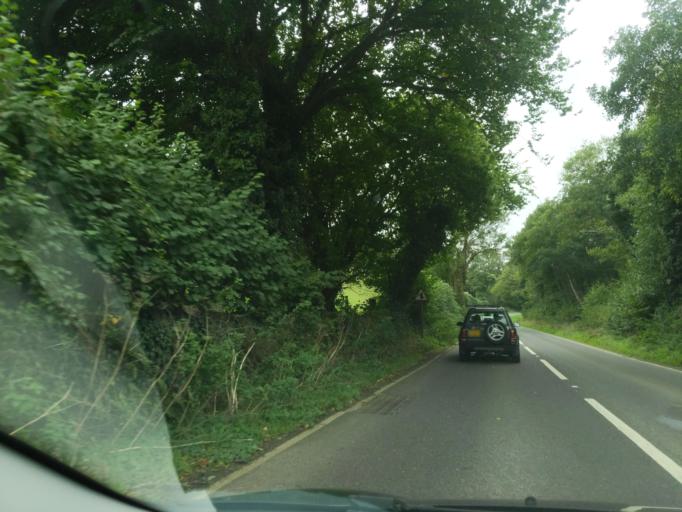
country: GB
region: England
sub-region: Cornwall
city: Wadebridge
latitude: 50.5082
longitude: -4.7996
